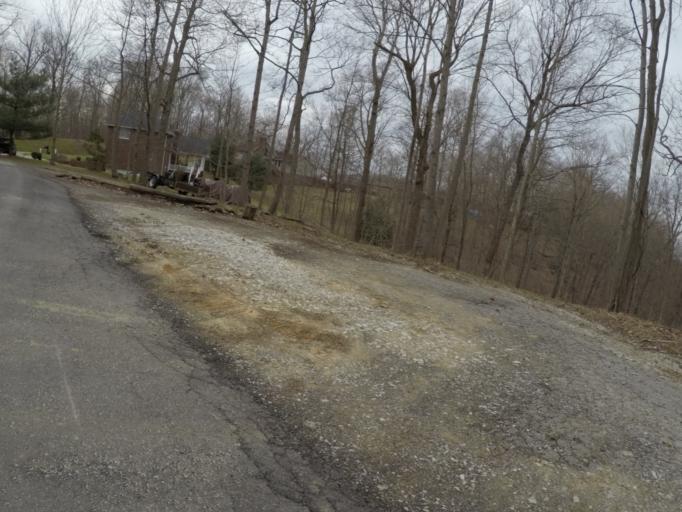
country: US
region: Ohio
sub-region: Lawrence County
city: Burlington
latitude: 38.3800
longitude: -82.5057
